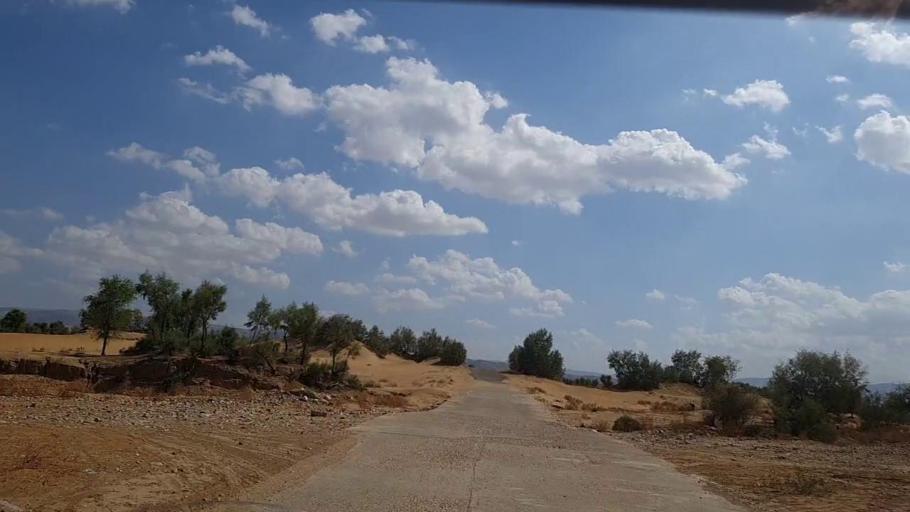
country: PK
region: Sindh
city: Johi
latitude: 26.5114
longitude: 67.4473
